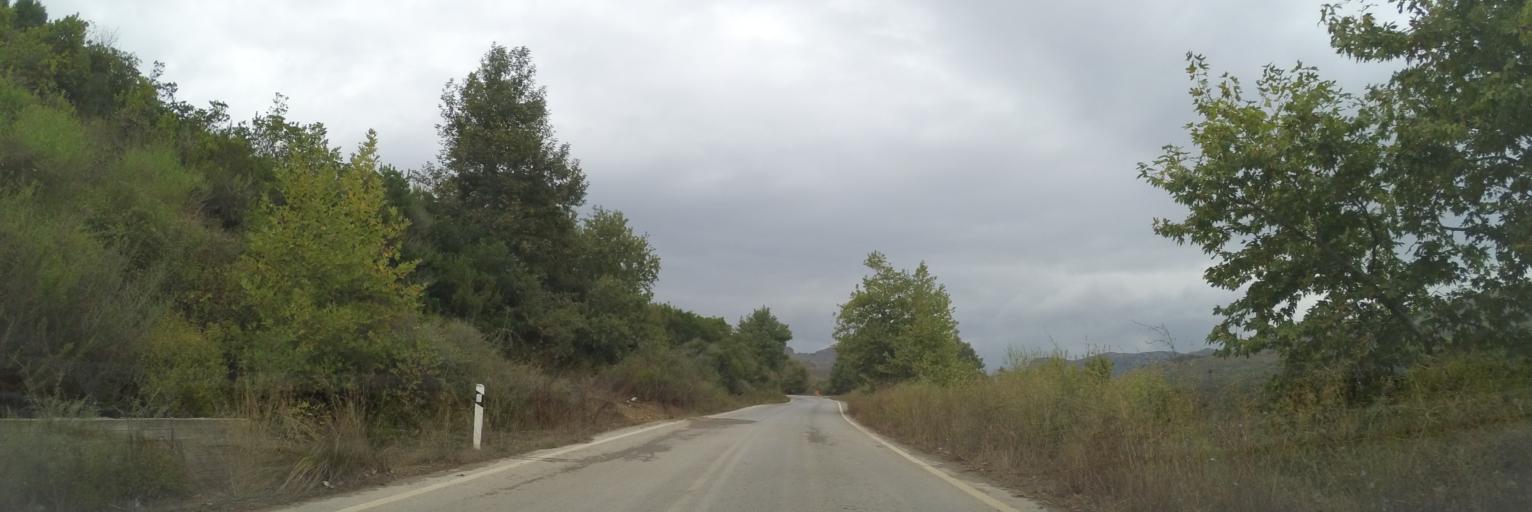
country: GR
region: Crete
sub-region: Nomos Rethymnis
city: Agia Foteini
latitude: 35.2899
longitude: 24.5629
